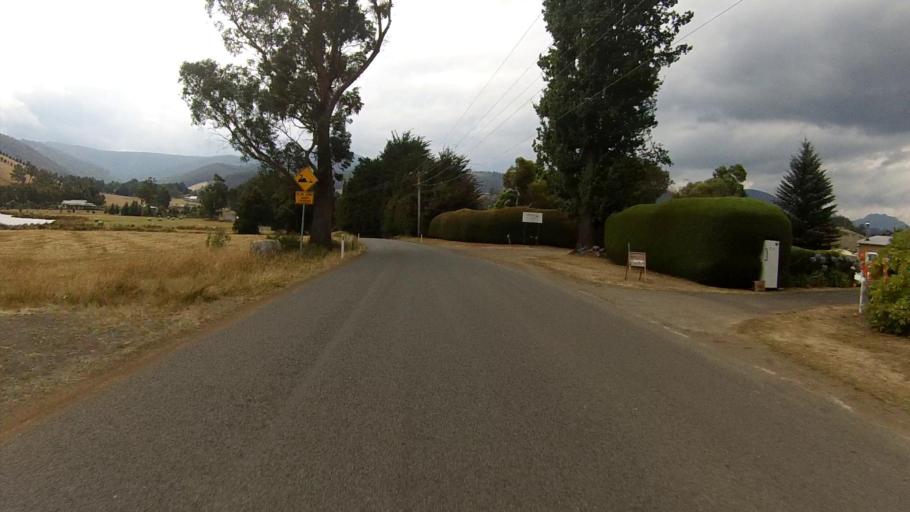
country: AU
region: Tasmania
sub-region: Huon Valley
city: Huonville
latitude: -42.9877
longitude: 147.0609
